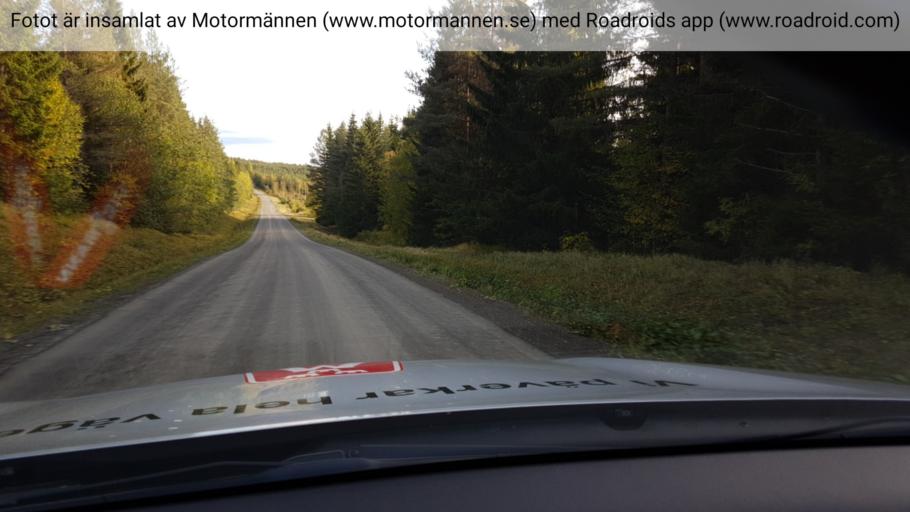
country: SE
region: Jaemtland
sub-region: Krokoms Kommun
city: Krokom
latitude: 63.6969
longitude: 14.5613
